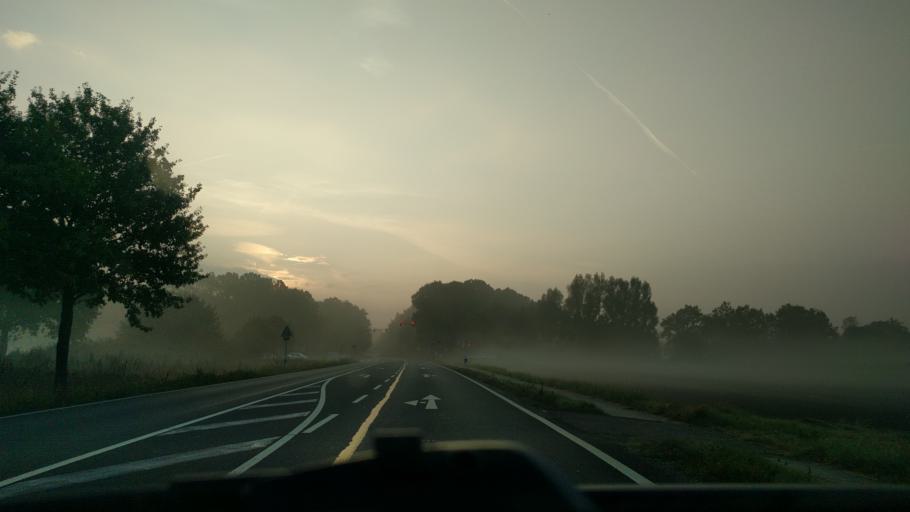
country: DE
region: Lower Saxony
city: Isenbuttel
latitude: 52.4405
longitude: 10.6016
